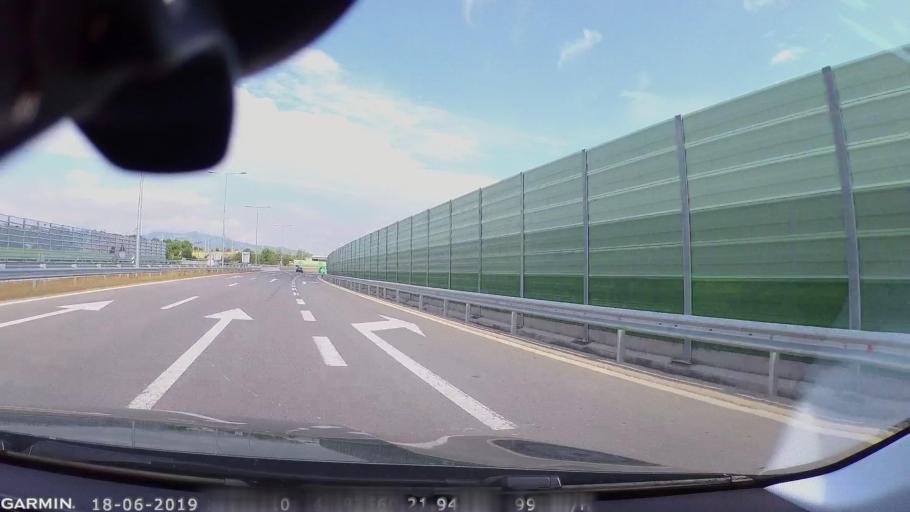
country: MK
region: Sveti Nikole
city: Sveti Nikole
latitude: 41.8756
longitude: 21.9418
